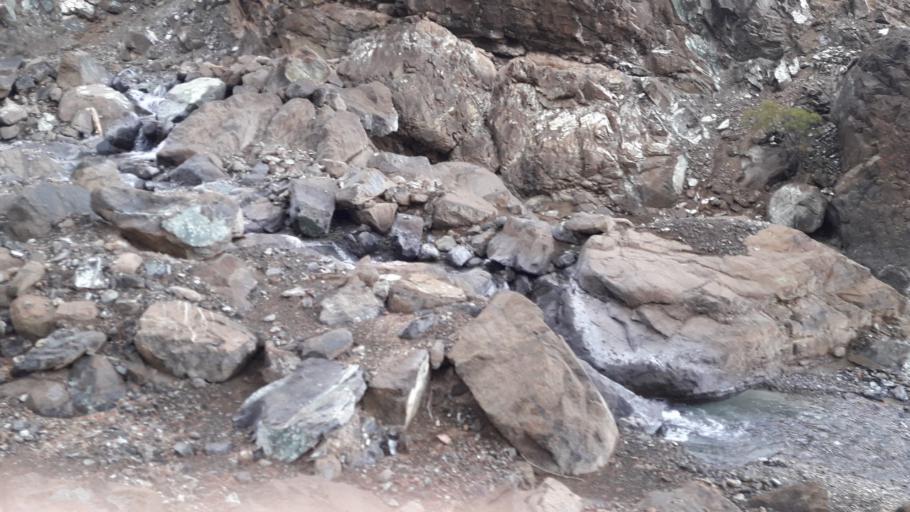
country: CY
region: Lefkosia
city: Kakopetria
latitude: 34.9511
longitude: 32.8843
